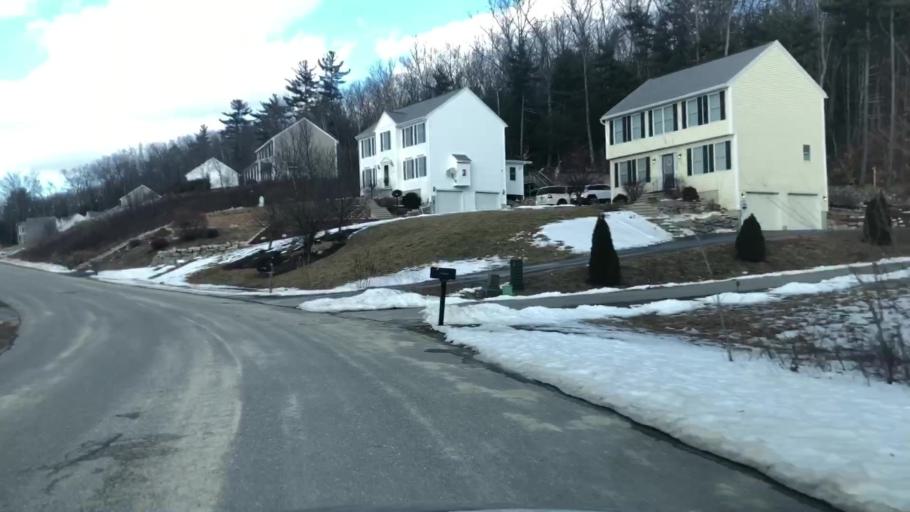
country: US
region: New Hampshire
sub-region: Hillsborough County
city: Milford
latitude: 42.8478
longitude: -71.6564
